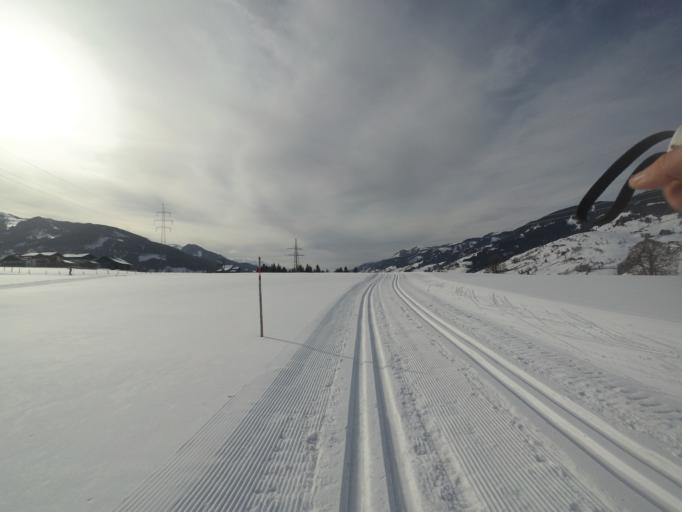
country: AT
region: Salzburg
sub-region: Politischer Bezirk Zell am See
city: Taxenbach
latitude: 47.2903
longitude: 12.9929
